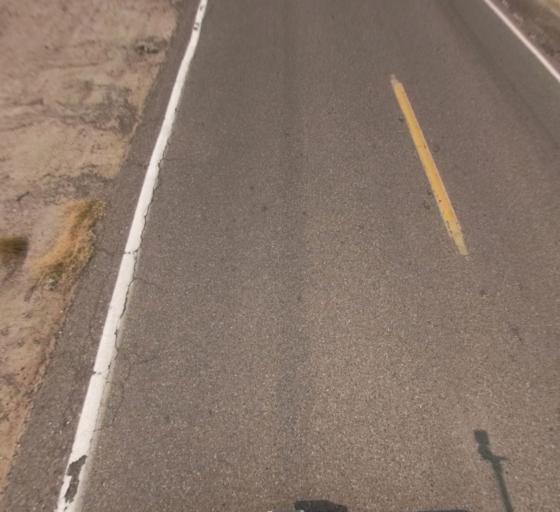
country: US
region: California
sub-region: Madera County
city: Fairmead
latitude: 37.1152
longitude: -120.1471
